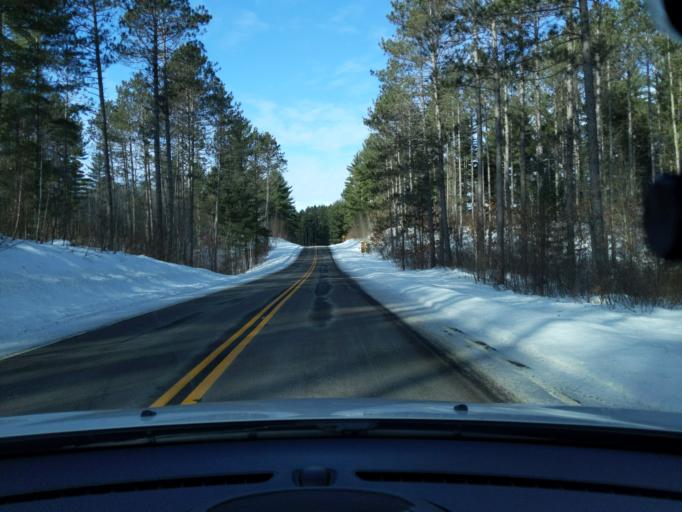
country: US
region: Wisconsin
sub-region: Sawyer County
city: Little Round Lake
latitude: 46.1100
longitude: -91.3039
